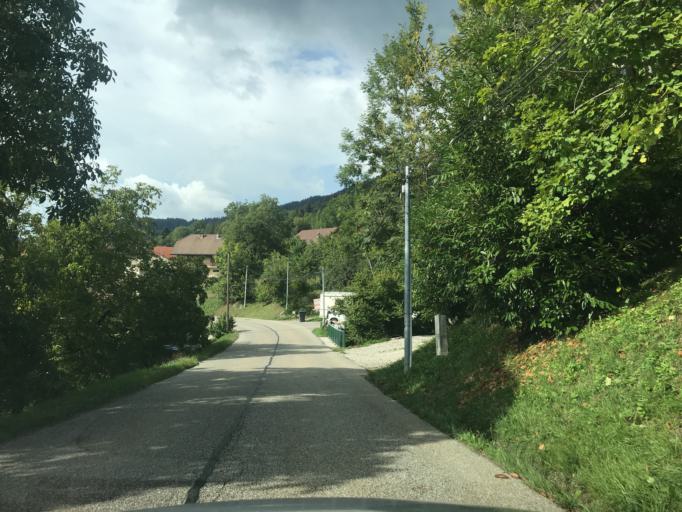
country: FR
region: Rhone-Alpes
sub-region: Departement de la Haute-Savoie
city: Talloires
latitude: 45.8362
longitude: 6.2324
